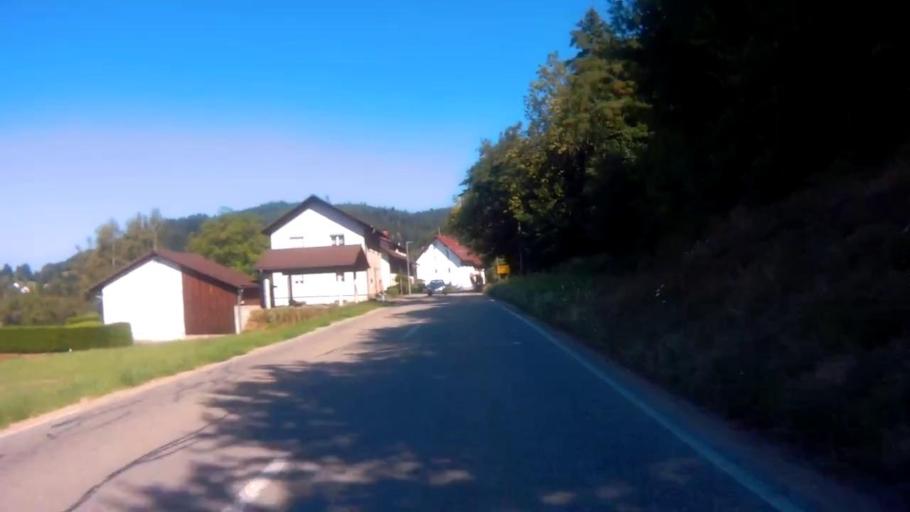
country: DE
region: Baden-Wuerttemberg
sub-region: Freiburg Region
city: Hausen
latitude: 47.6862
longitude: 7.8036
